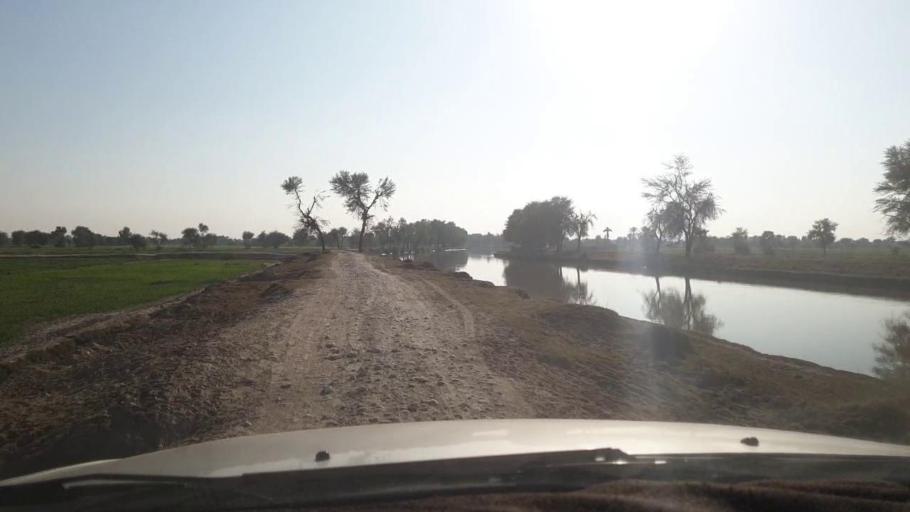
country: PK
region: Sindh
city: Mirpur Mathelo
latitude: 27.9674
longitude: 69.5225
